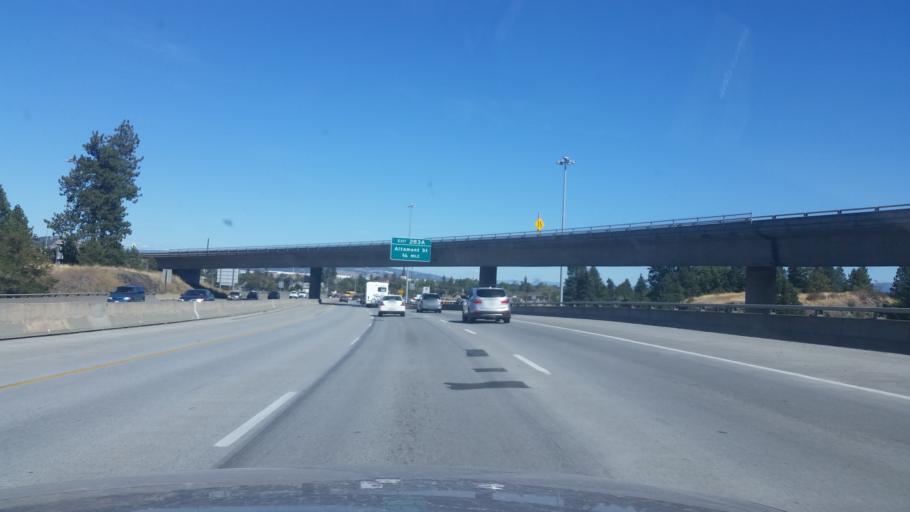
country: US
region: Washington
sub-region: Spokane County
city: Spokane
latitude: 47.6522
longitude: -117.3936
